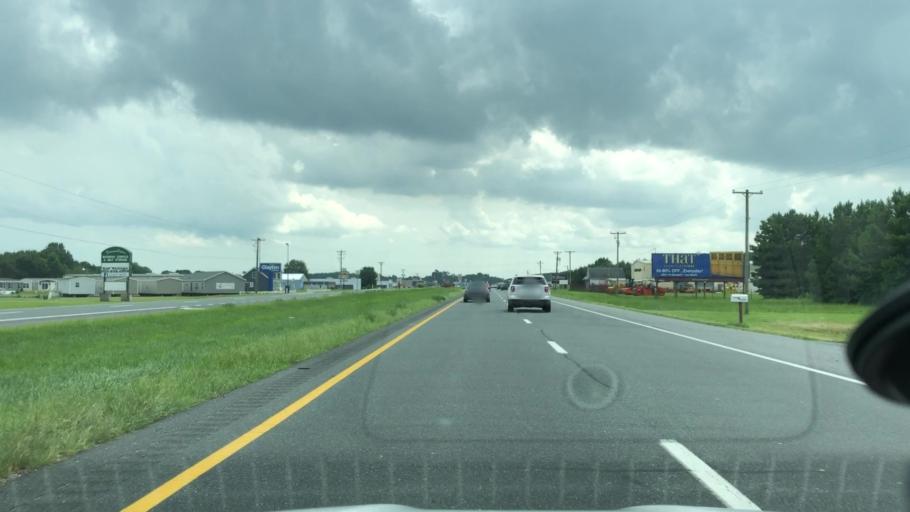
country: US
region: Delaware
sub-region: Sussex County
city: Delmar
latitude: 38.4659
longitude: -75.5582
